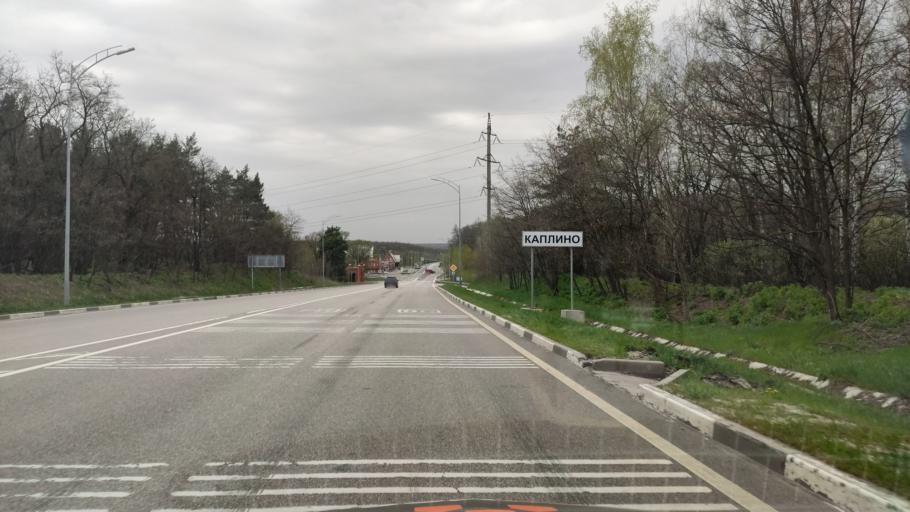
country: RU
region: Belgorod
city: Staryy Oskol
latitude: 51.3585
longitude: 37.8350
